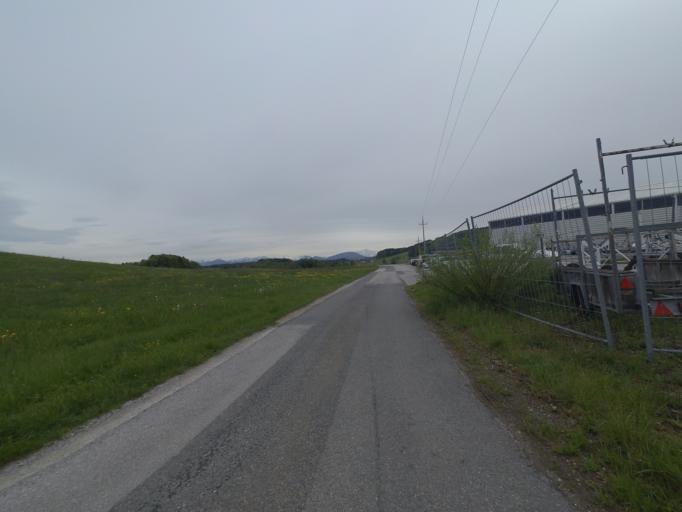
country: AT
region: Salzburg
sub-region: Politischer Bezirk Salzburg-Umgebung
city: Mattsee
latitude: 47.9714
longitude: 13.1246
